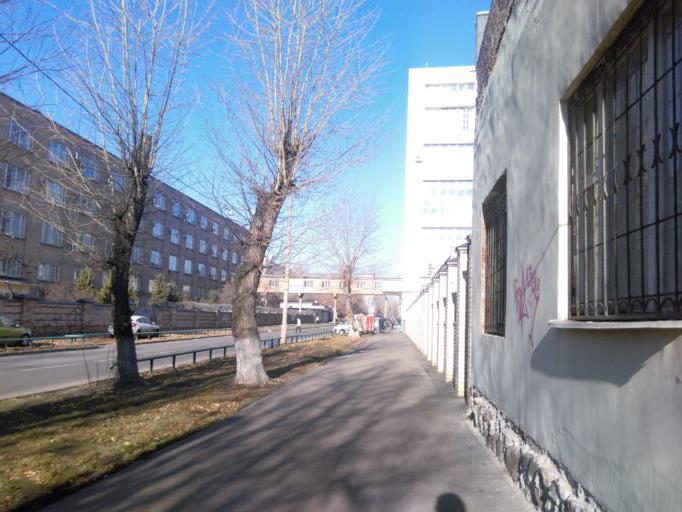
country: RU
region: Moscow
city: Mar'ina Roshcha
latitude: 55.7970
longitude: 37.5862
